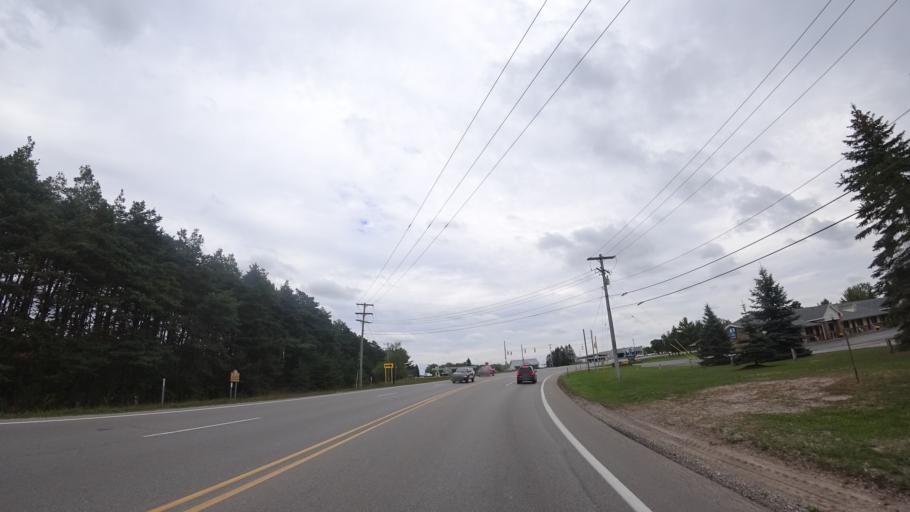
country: US
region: Michigan
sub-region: Emmet County
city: Petoskey
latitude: 45.4279
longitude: -84.9069
